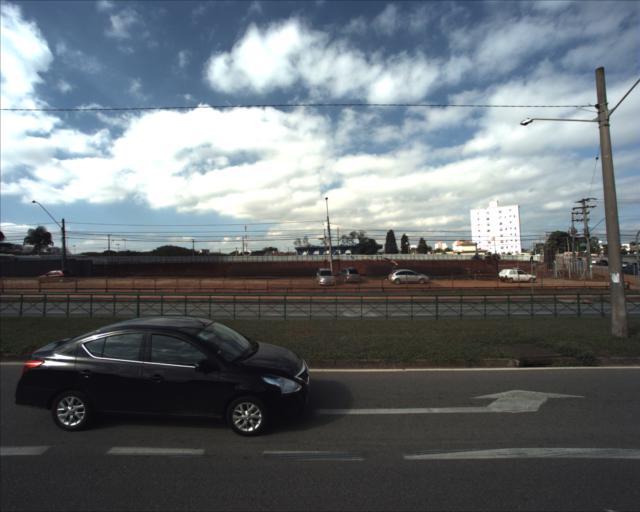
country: BR
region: Sao Paulo
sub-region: Sorocaba
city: Sorocaba
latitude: -23.5277
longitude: -47.4902
